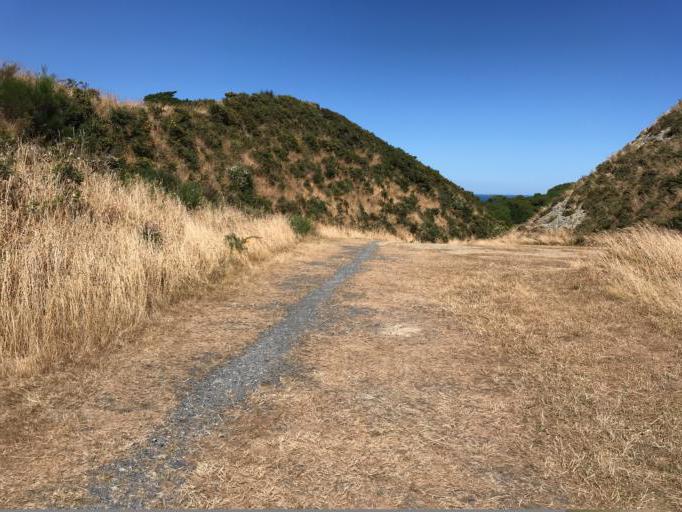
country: NZ
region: Wellington
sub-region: Wellington City
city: Brooklyn
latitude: -41.3323
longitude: 174.7662
